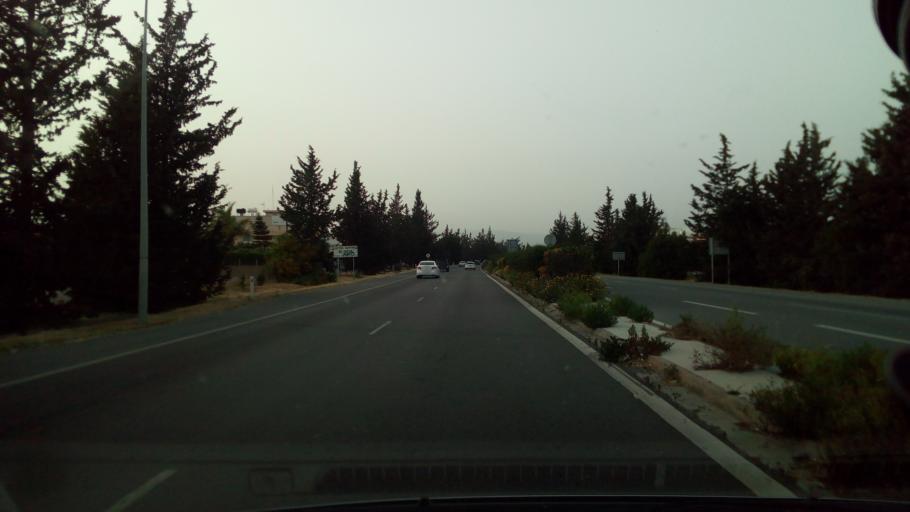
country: CY
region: Limassol
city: Limassol
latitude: 34.6807
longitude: 33.0092
